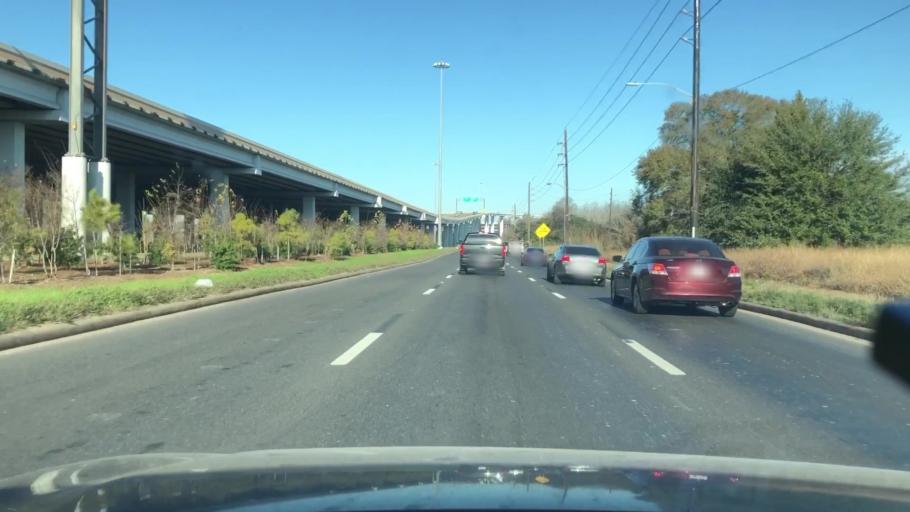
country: US
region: Texas
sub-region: Fort Bend County
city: Meadows Place
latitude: 29.6549
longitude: -95.5510
